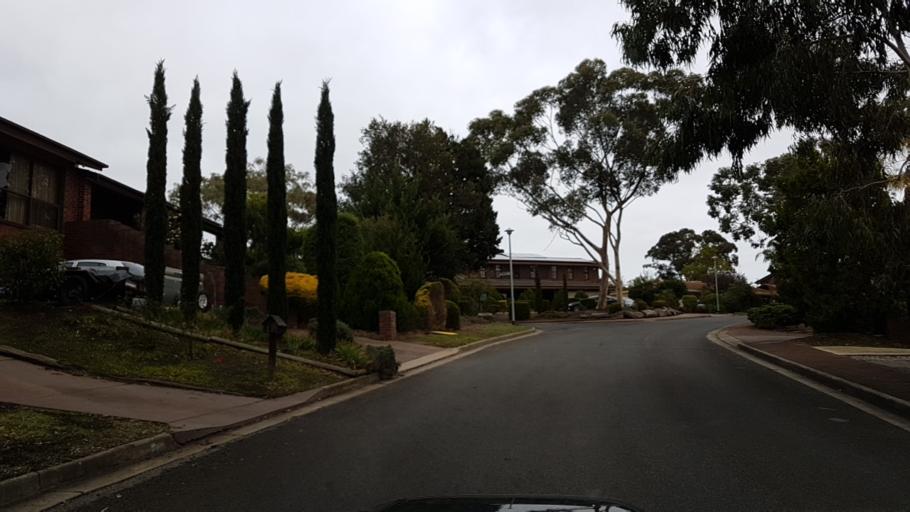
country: AU
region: South Australia
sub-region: Onkaparinga
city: Bedford Park
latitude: -35.0477
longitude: 138.5868
